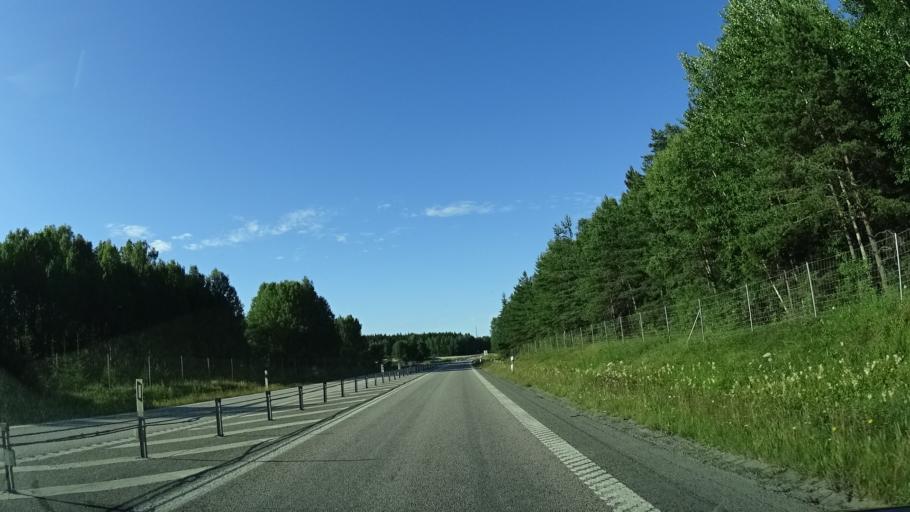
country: SE
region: Stockholm
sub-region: Vallentuna Kommun
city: Vallentuna
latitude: 59.5143
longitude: 18.1773
